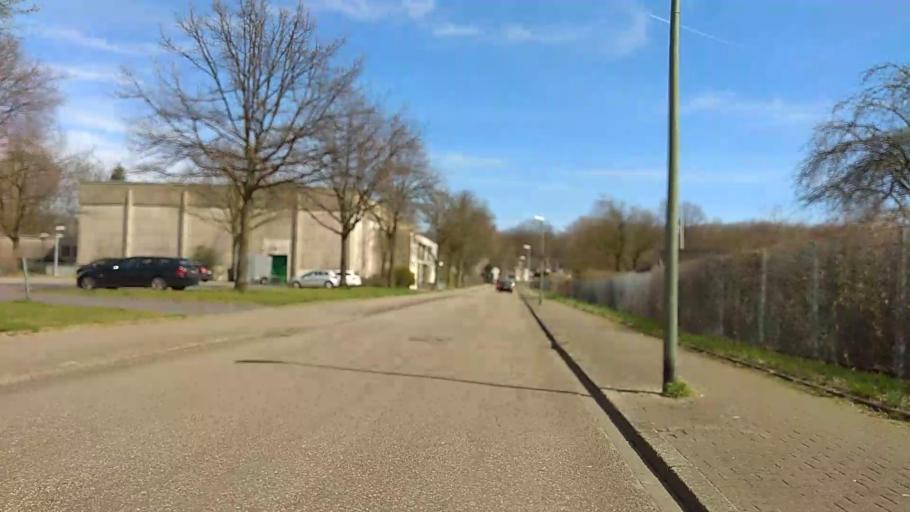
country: DE
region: North Rhine-Westphalia
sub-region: Regierungsbezirk Munster
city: Gelsenkirchen
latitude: 51.5586
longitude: 7.0978
